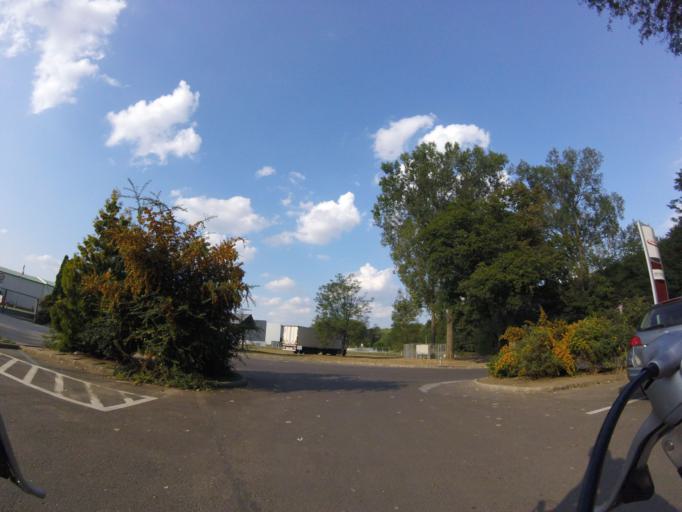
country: HU
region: Szabolcs-Szatmar-Bereg
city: Nyirkarasz
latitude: 48.0808
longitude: 22.0899
